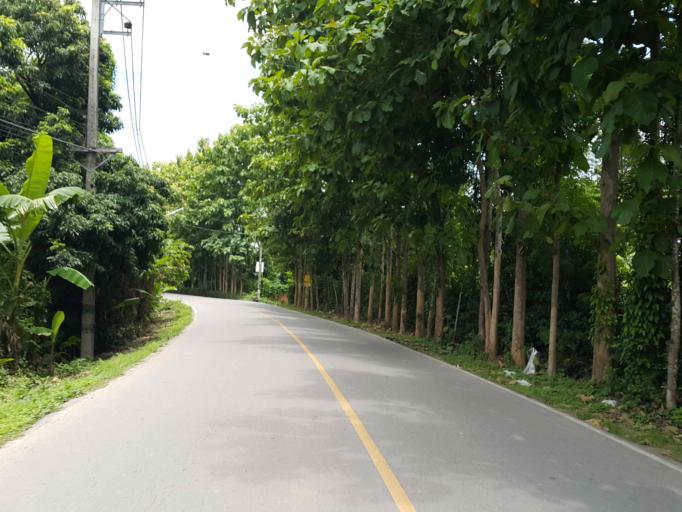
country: TH
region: Chiang Mai
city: San Sai
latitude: 18.8586
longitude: 98.9850
